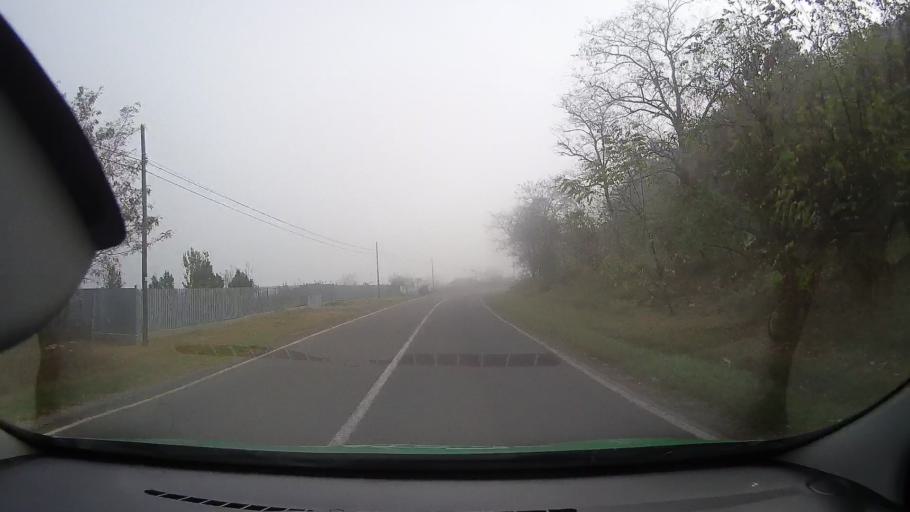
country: RO
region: Tulcea
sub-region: Municipiul Tulcea
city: Tulcea
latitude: 45.1676
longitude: 28.8353
